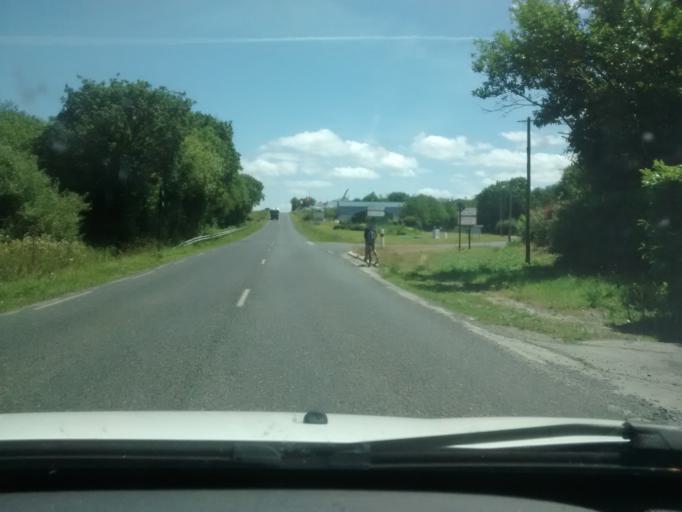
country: FR
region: Brittany
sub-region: Departement des Cotes-d'Armor
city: Trelevern
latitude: 48.7770
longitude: -3.3770
